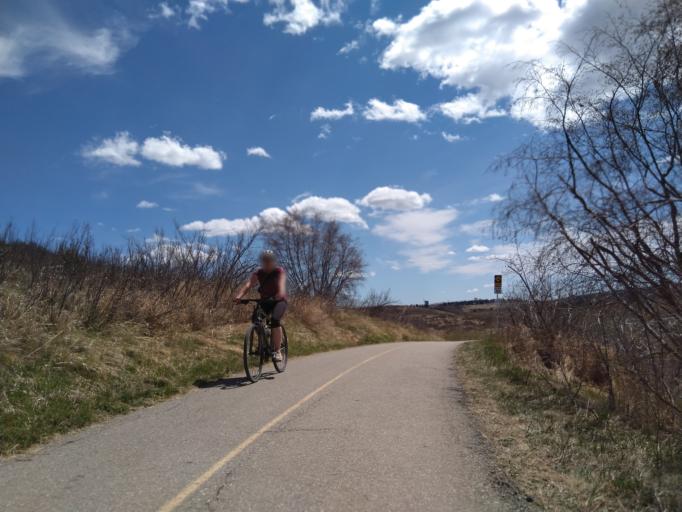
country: CA
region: Alberta
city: Calgary
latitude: 51.0970
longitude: -114.1876
